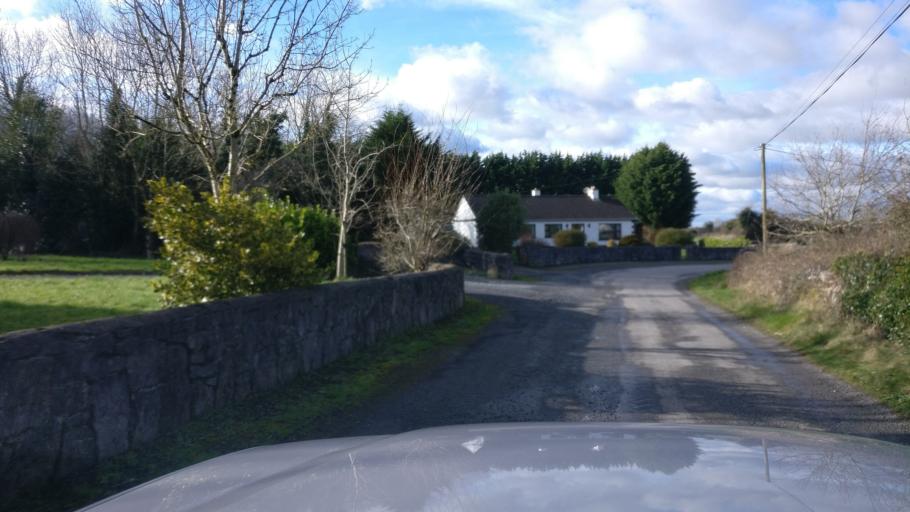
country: IE
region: Connaught
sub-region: County Galway
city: Athenry
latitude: 53.2271
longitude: -8.7986
